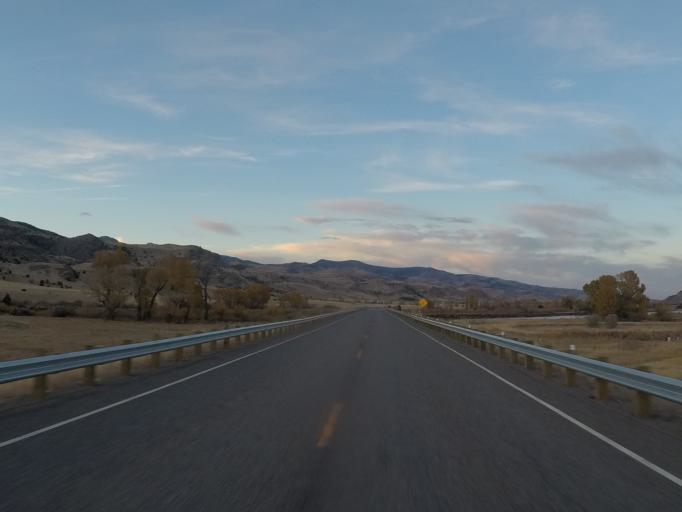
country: US
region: Montana
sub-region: Gallatin County
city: Bozeman
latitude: 45.2510
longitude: -110.8689
